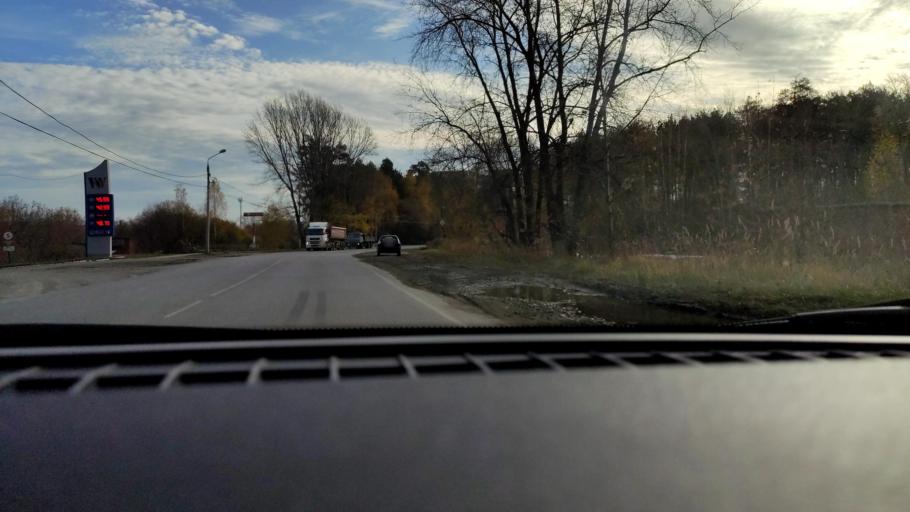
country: RU
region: Perm
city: Overyata
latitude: 58.0128
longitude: 55.9216
